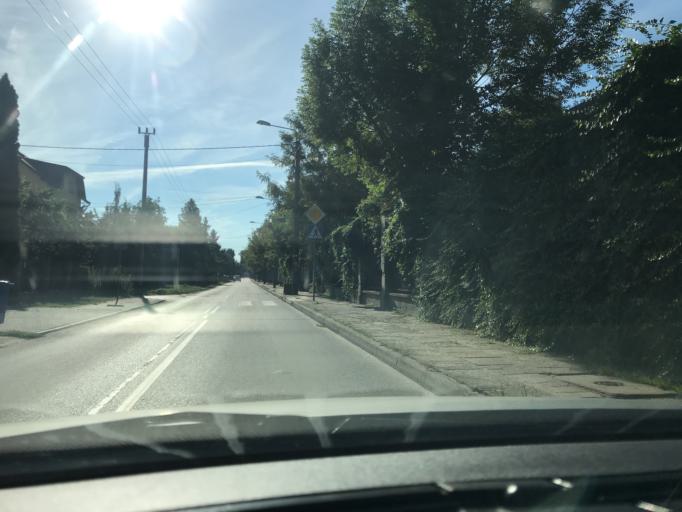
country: PL
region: Masovian Voivodeship
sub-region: Powiat pruszkowski
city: Piastow
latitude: 52.1700
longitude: 20.8315
